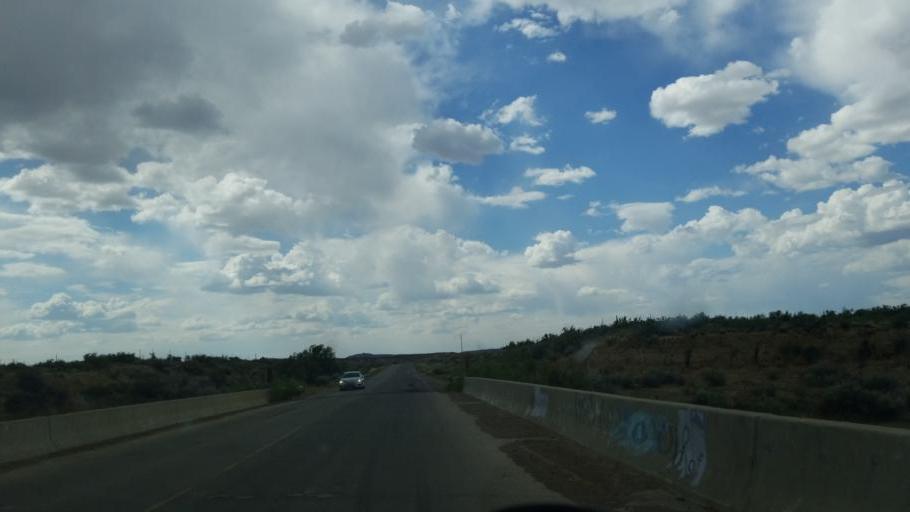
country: US
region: New Mexico
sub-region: McKinley County
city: Gallup
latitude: 35.4902
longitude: -108.9055
